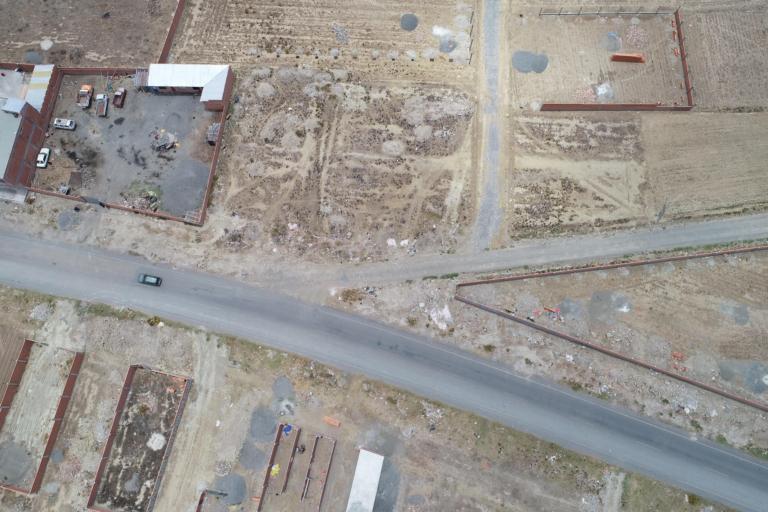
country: BO
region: La Paz
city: Achacachi
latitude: -16.0459
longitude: -68.6934
